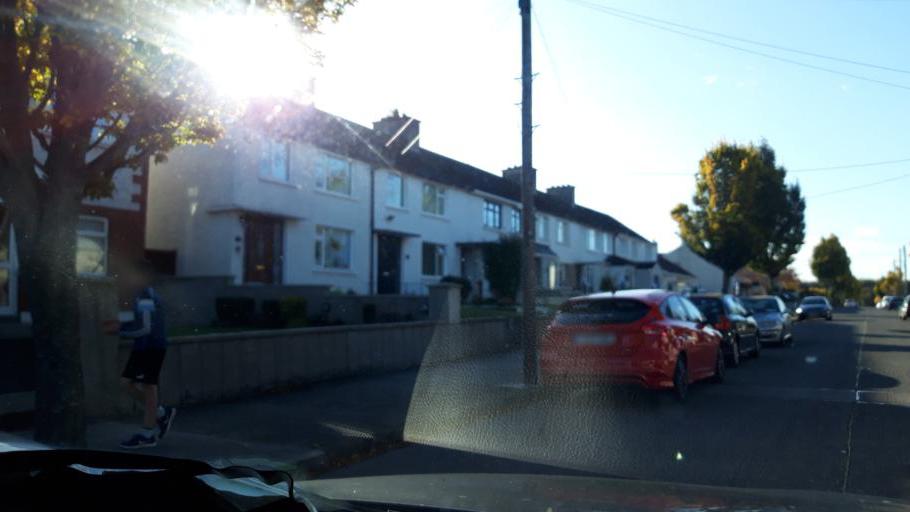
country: IE
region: Leinster
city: Raheny
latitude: 53.3770
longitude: -6.1838
